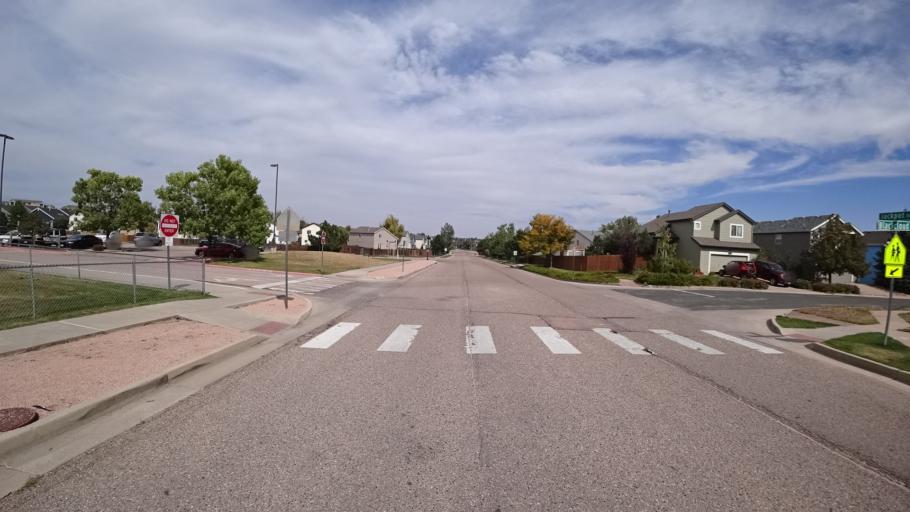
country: US
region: Colorado
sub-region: El Paso County
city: Cimarron Hills
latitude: 38.9053
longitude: -104.7112
